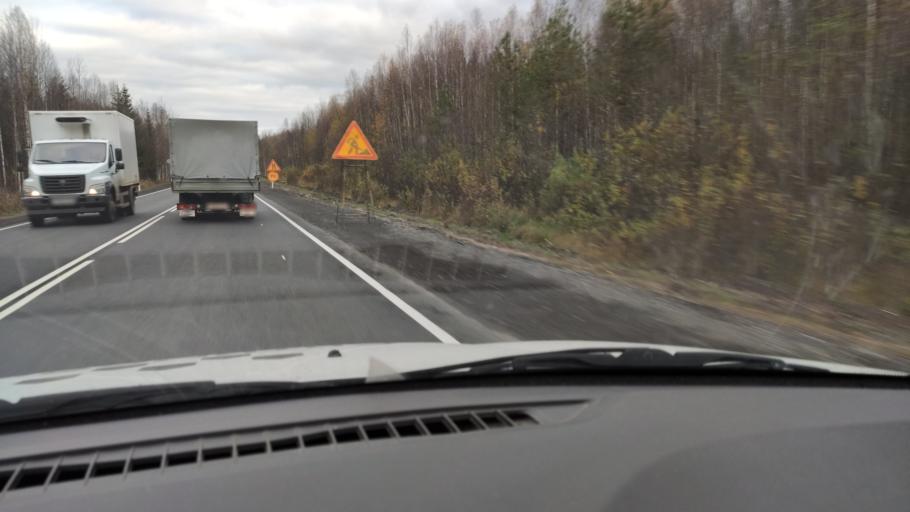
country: RU
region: Kirov
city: Chernaya Kholunitsa
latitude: 58.8747
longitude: 51.4913
